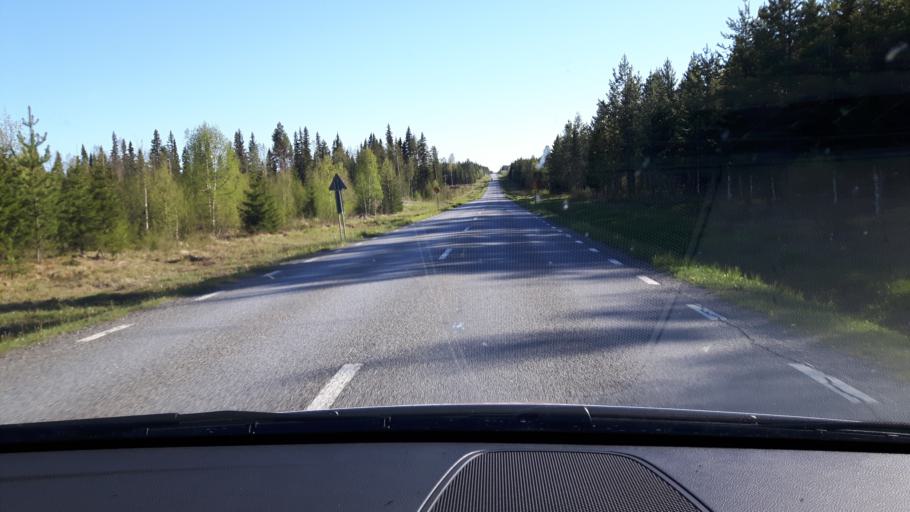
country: SE
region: Jaemtland
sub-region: Stroemsunds Kommun
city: Stroemsund
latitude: 63.7245
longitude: 15.4783
